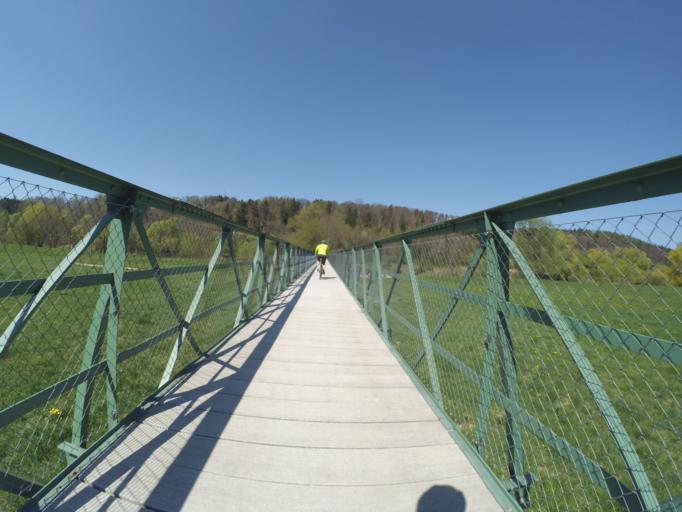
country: CH
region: Thurgau
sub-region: Frauenfeld District
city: Frauenfeld
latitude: 47.5827
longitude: 8.9033
